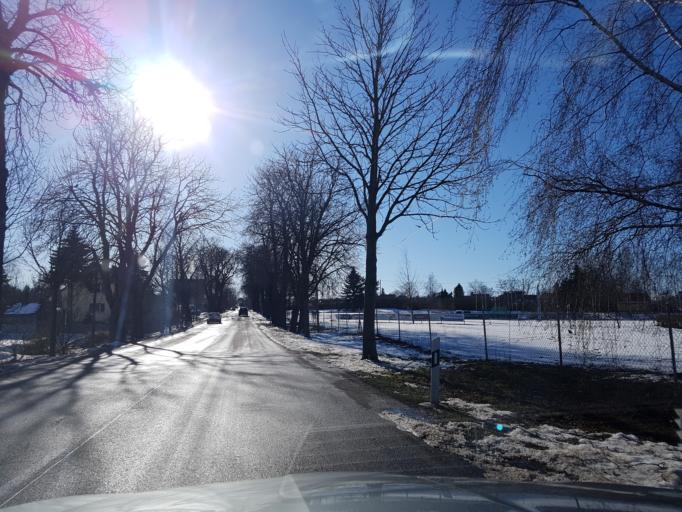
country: DE
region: Saxony
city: Moritzburg
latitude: 51.1285
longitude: 13.6863
